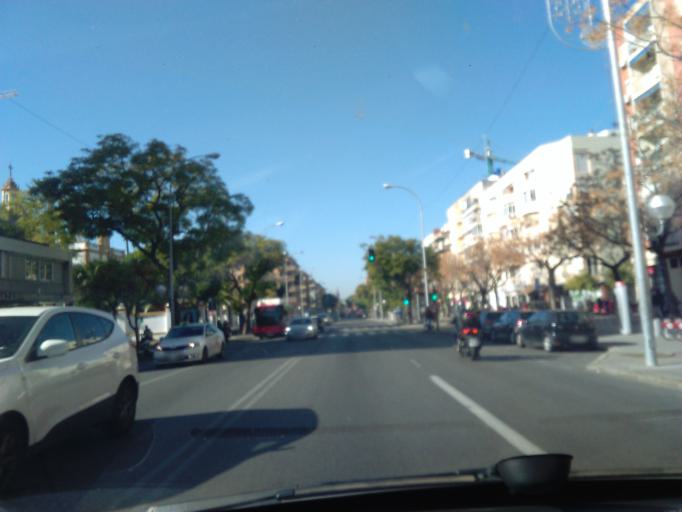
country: ES
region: Andalusia
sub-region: Provincia de Sevilla
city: Sevilla
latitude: 37.3819
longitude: -5.9678
